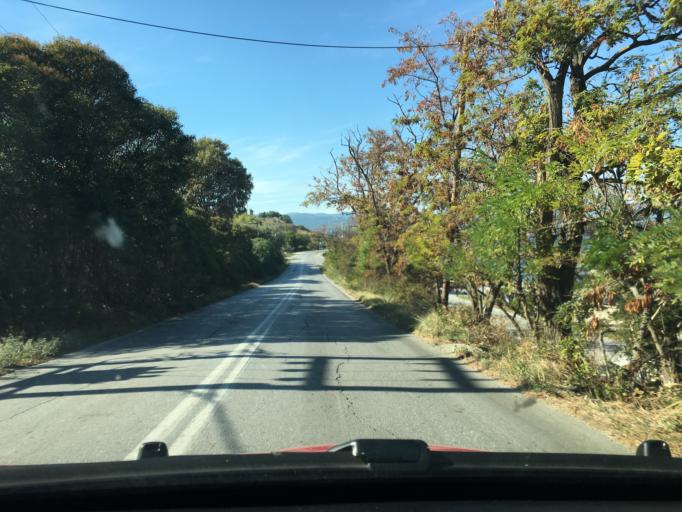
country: GR
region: Central Macedonia
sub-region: Nomos Chalkidikis
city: Ierissos
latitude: 40.3930
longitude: 23.8931
